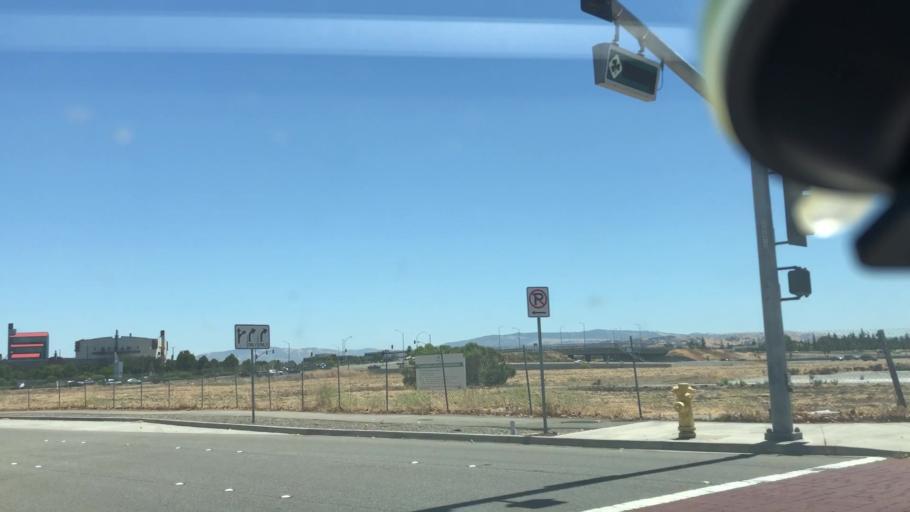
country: US
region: California
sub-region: Alameda County
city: Dublin
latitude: 37.7046
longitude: -121.8908
